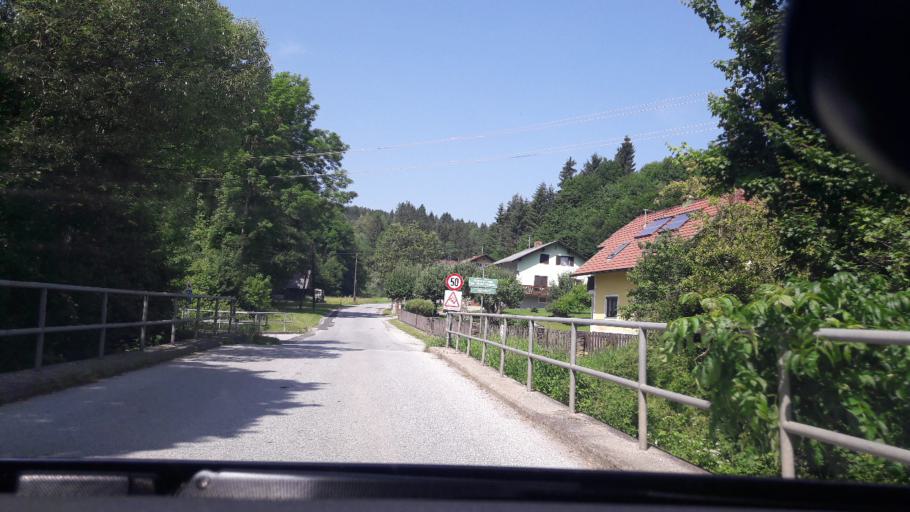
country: AT
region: Styria
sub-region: Politischer Bezirk Voitsberg
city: Sodingberg
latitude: 47.1084
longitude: 15.1714
